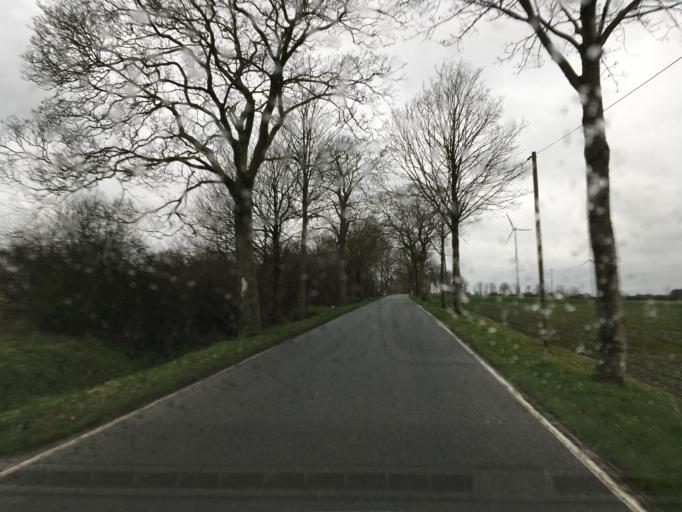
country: DE
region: North Rhine-Westphalia
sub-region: Regierungsbezirk Munster
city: Schoppingen
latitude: 52.0784
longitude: 7.1656
